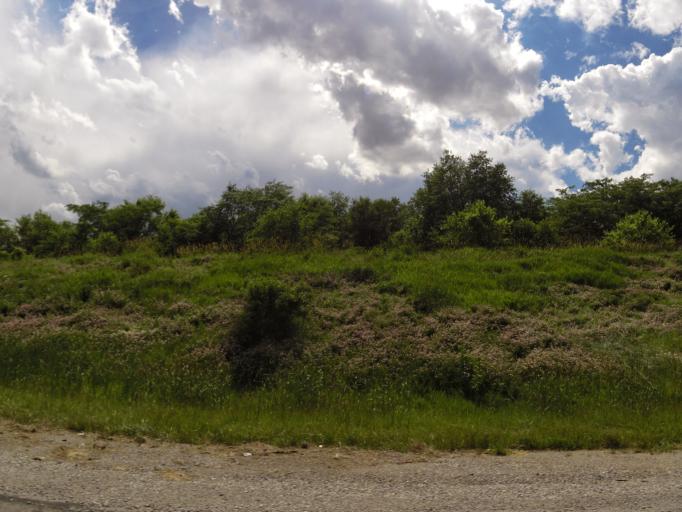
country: US
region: Iowa
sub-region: Johnson County
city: University Heights
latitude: 41.6159
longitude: -91.5512
